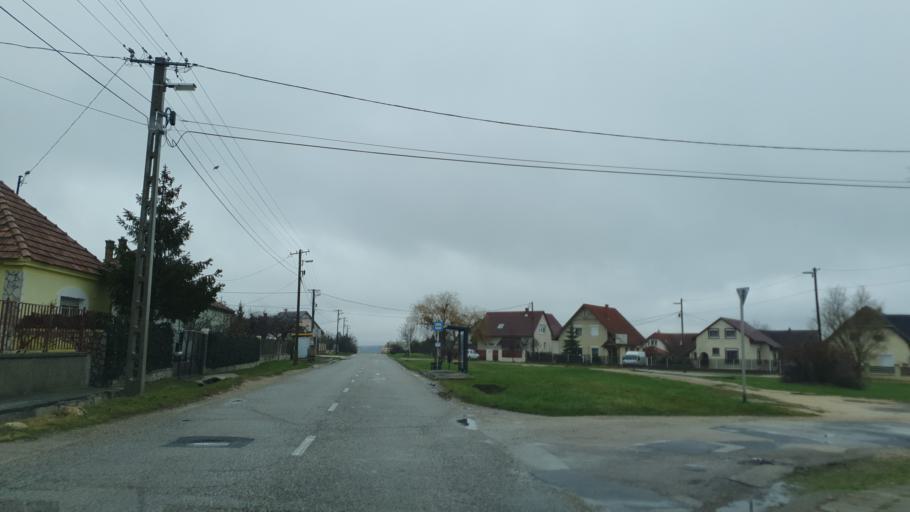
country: HU
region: Veszprem
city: Hajmasker
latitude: 47.1437
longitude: 17.9554
